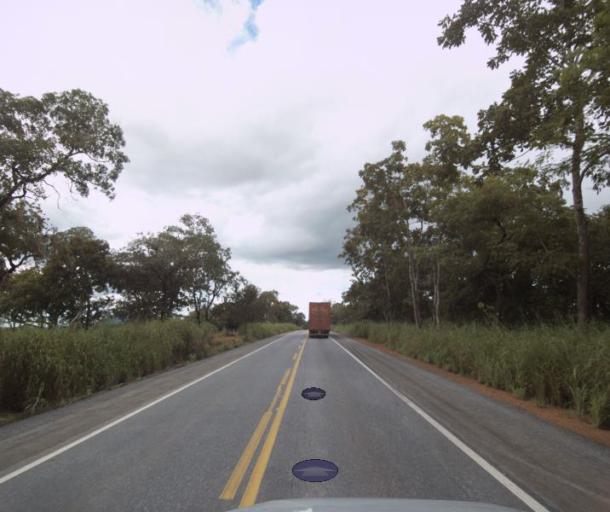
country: BR
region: Goias
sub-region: Porangatu
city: Porangatu
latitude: -13.2964
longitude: -49.1228
